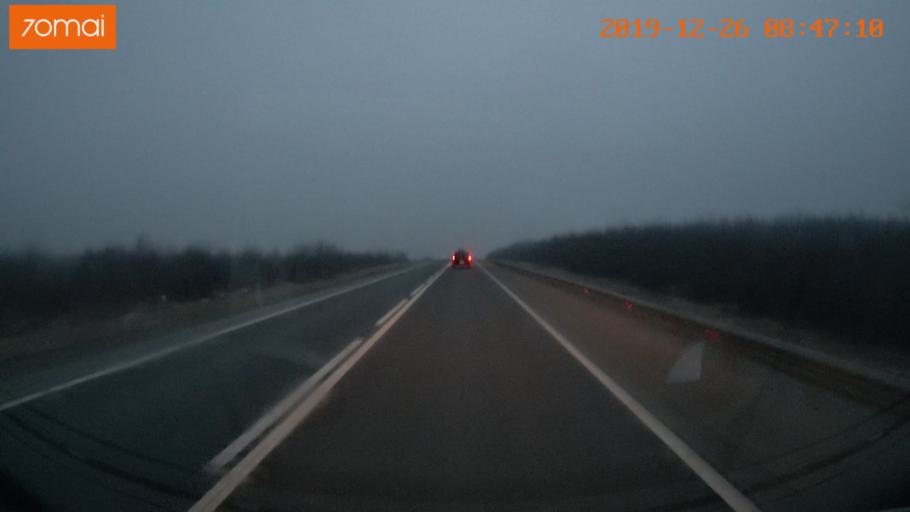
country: RU
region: Jaroslavl
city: Prechistoye
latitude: 58.6198
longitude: 40.3329
